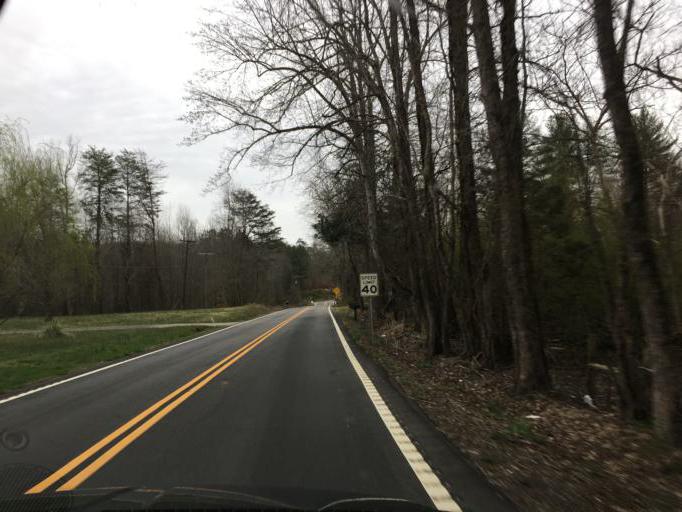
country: US
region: South Carolina
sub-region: Greenville County
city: Berea
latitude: 34.9331
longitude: -82.5093
